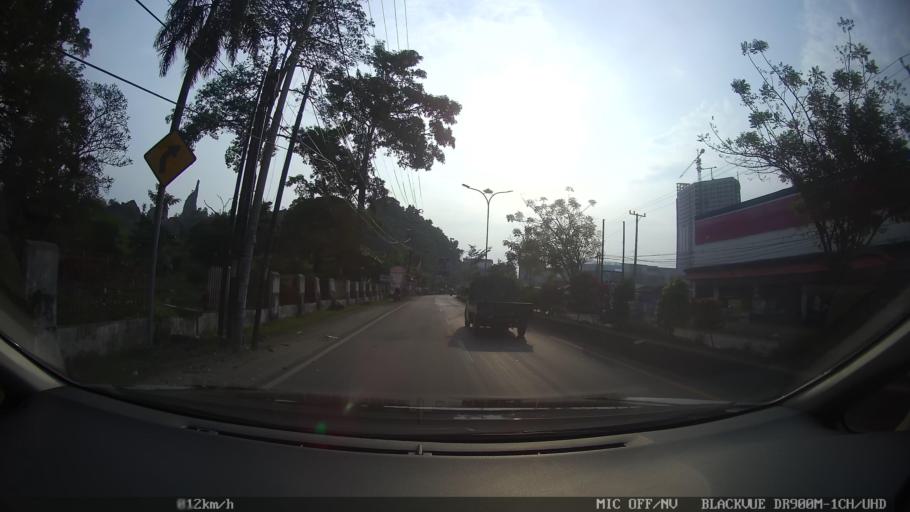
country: ID
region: Lampung
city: Bandarlampung
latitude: -5.4441
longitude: 105.2838
